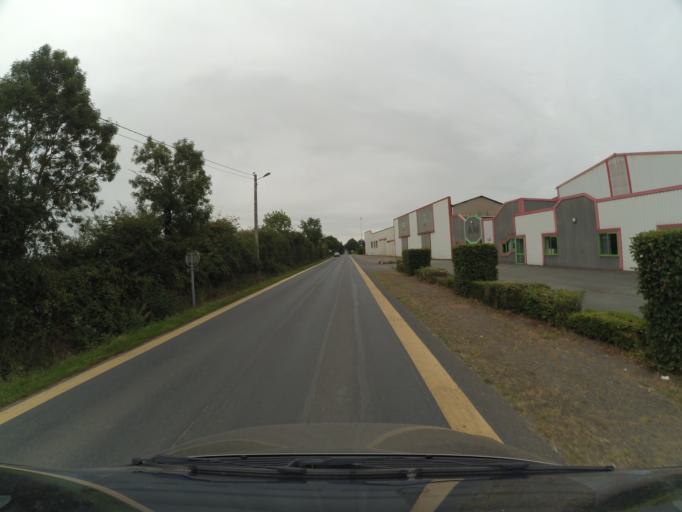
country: FR
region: Pays de la Loire
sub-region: Departement de la Vendee
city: Saint-Andre-Treize-Voies
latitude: 46.9354
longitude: -1.4059
